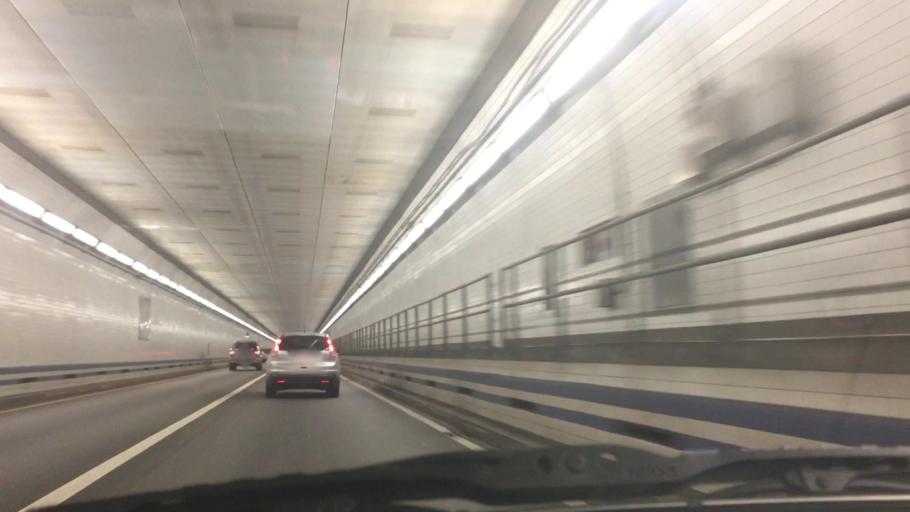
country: US
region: Virginia
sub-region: City of Hampton
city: East Hampton
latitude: 36.9870
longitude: -76.3058
